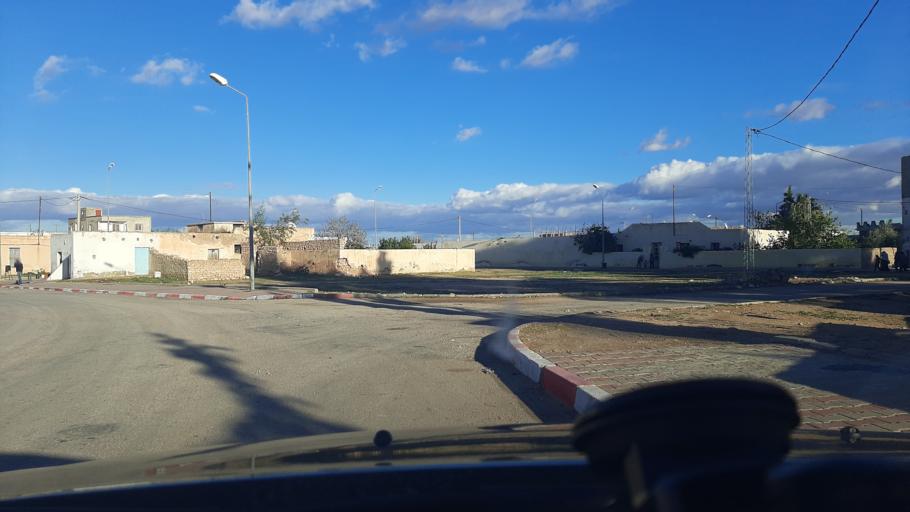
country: TN
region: Al Mahdiyah
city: Shurban
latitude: 34.9609
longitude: 10.3631
